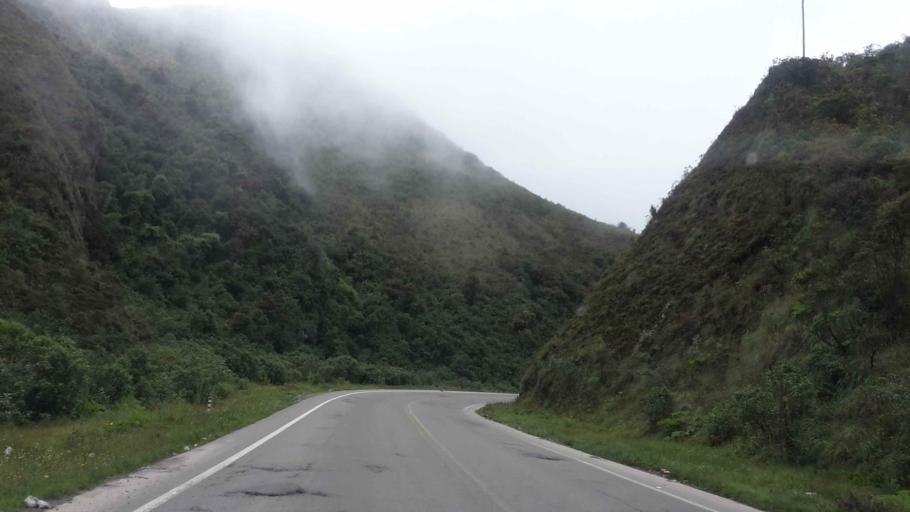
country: BO
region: Cochabamba
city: Colomi
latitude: -17.2170
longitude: -65.8922
